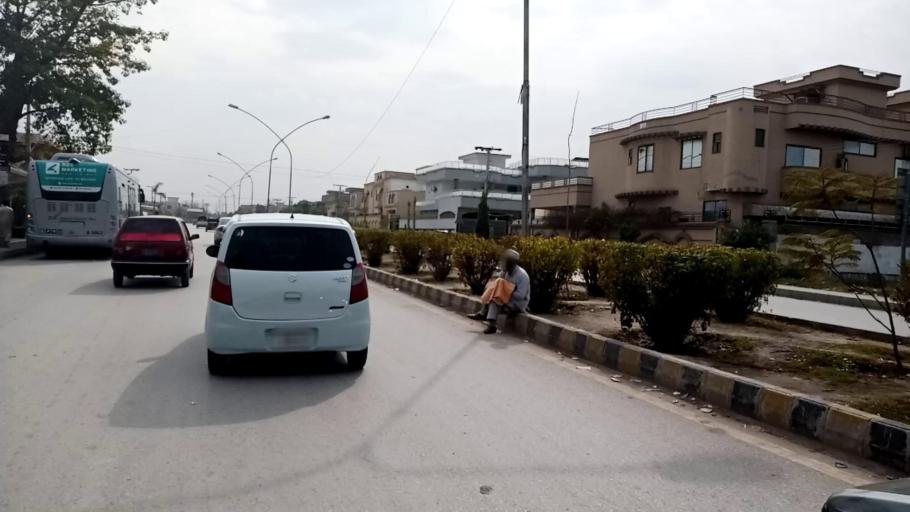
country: PK
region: Khyber Pakhtunkhwa
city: Peshawar
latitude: 33.9591
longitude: 71.4434
